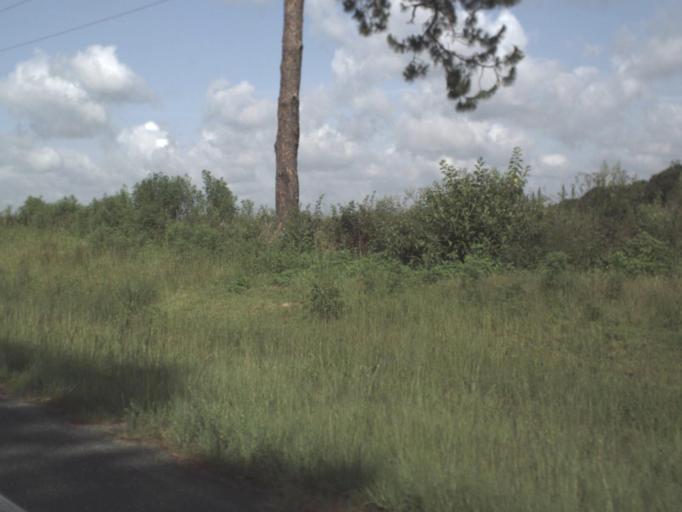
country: US
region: Florida
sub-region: Suwannee County
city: Wellborn
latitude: 30.0884
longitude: -82.7591
